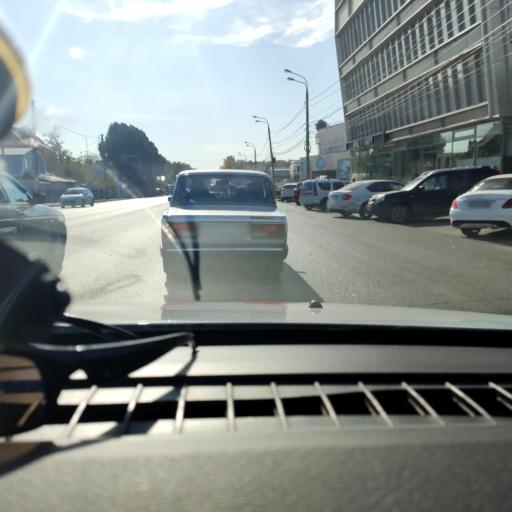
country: RU
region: Samara
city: Samara
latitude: 53.1988
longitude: 50.1902
